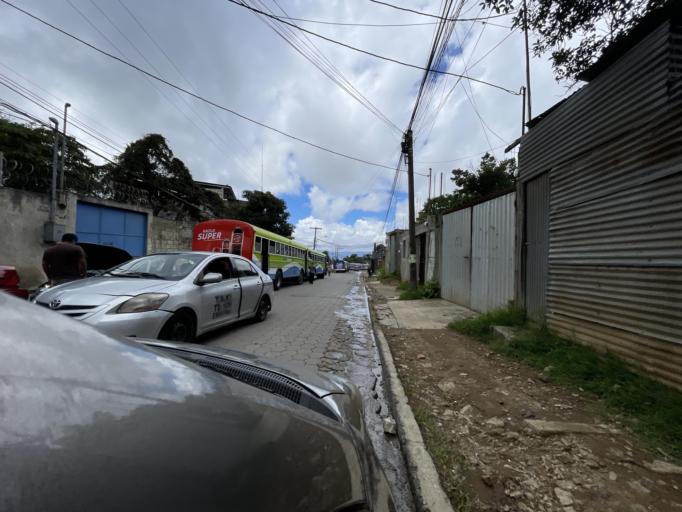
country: GT
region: Guatemala
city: Mixco
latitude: 14.6366
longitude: -90.6191
